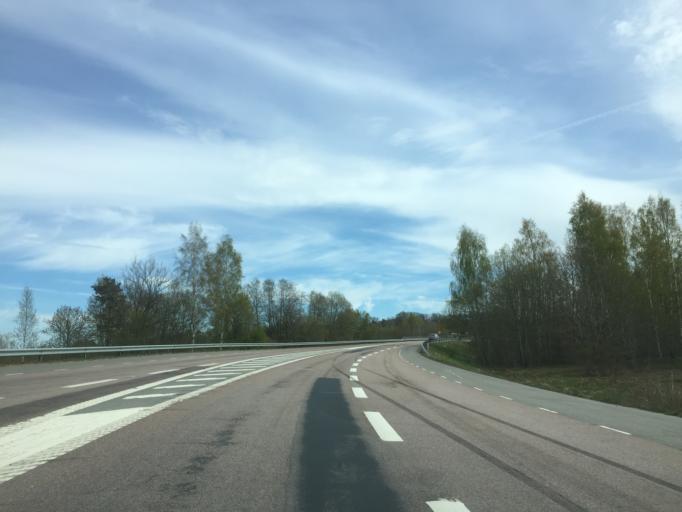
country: SE
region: OErebro
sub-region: Askersunds Kommun
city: Asbro
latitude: 59.0452
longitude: 14.9304
